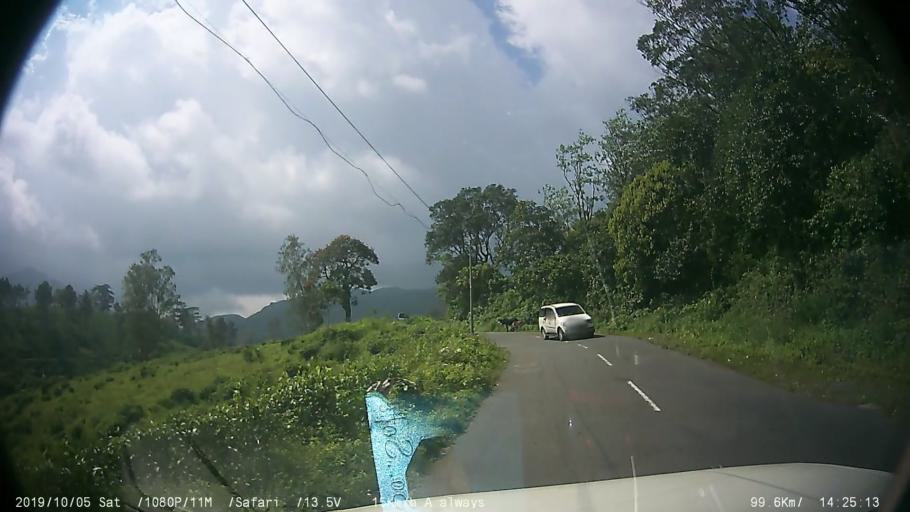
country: IN
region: Kerala
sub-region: Kottayam
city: Erattupetta
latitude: 9.5949
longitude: 76.9698
